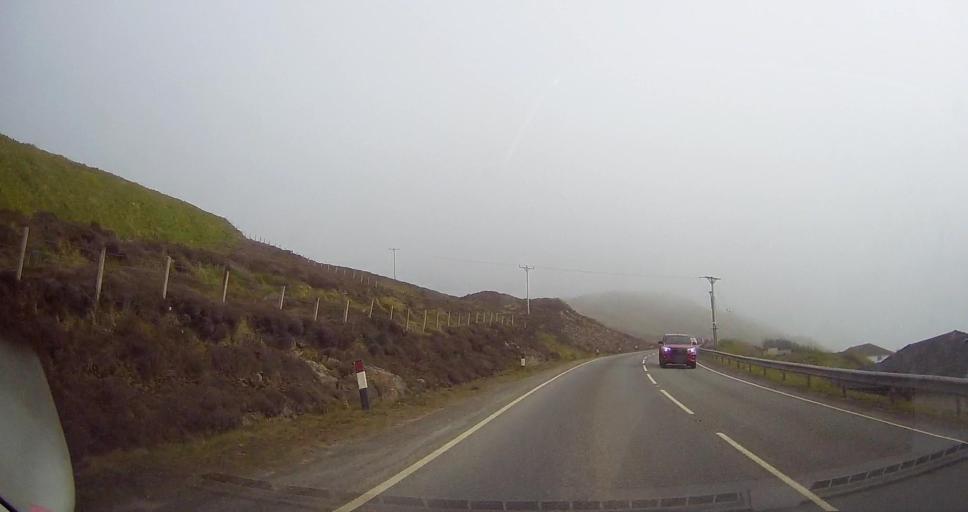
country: GB
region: Scotland
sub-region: Shetland Islands
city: Lerwick
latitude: 60.1420
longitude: -1.2615
